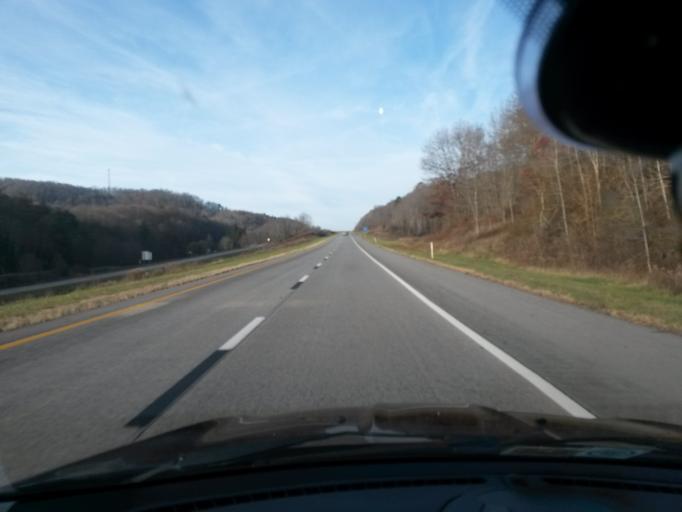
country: US
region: West Virginia
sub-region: Greenbrier County
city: Rainelle
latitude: 37.8428
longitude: -80.7381
